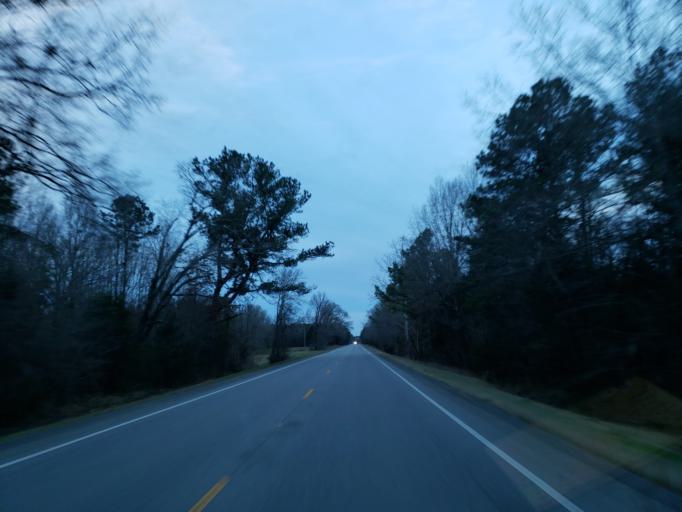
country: US
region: Alabama
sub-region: Sumter County
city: Livingston
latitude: 32.8208
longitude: -88.3105
